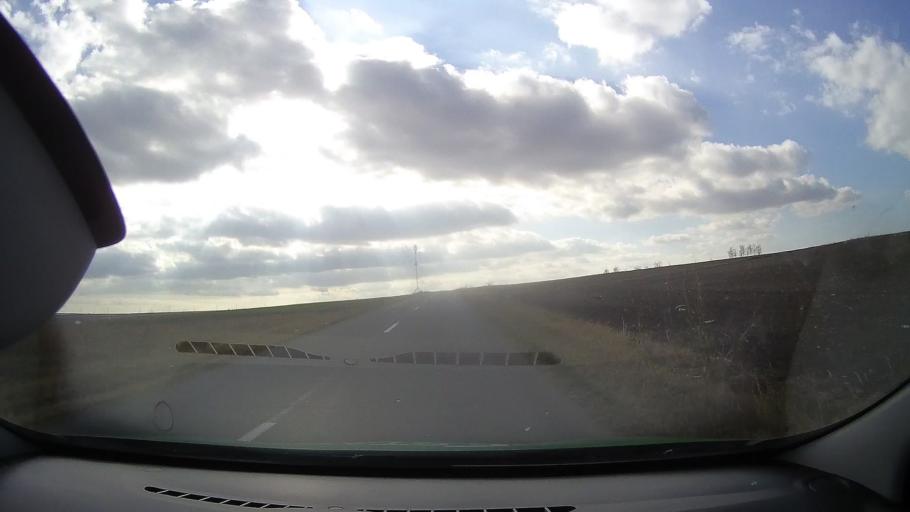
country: RO
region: Constanta
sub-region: Comuna Sacele
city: Sacele
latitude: 44.4944
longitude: 28.6561
